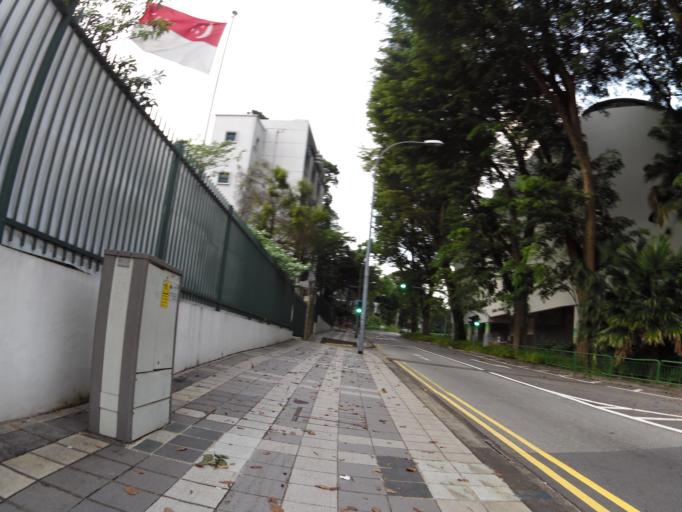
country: SG
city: Singapore
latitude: 1.2931
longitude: 103.8487
